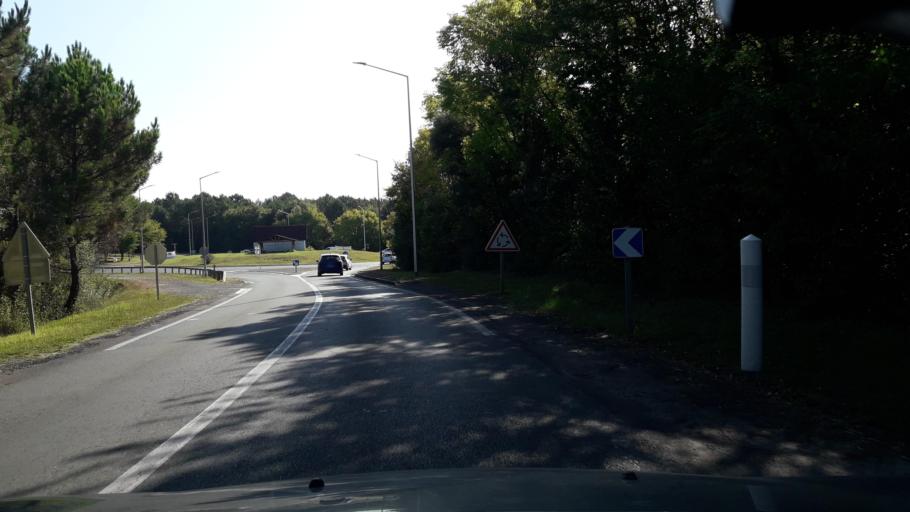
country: FR
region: Poitou-Charentes
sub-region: Departement de la Charente-Maritime
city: Etaules
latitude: 45.7209
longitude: -1.0811
